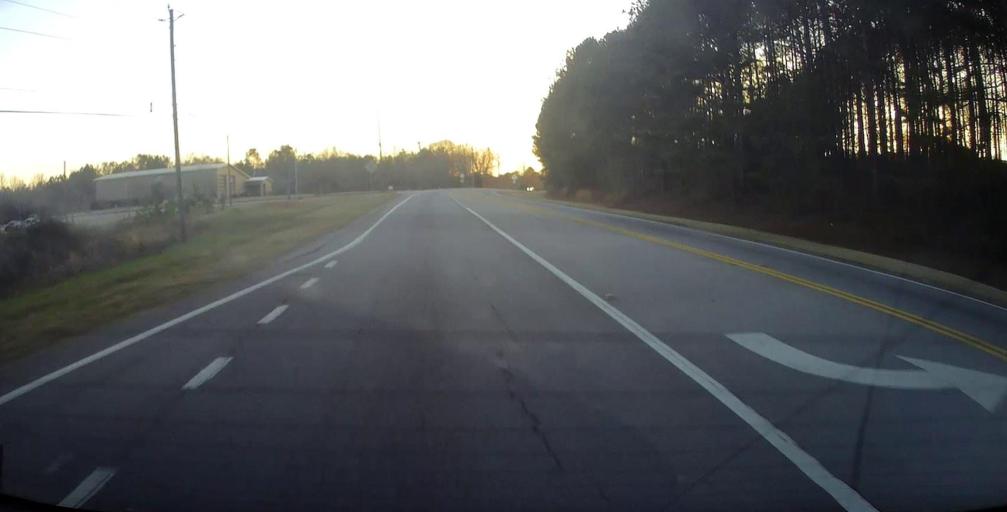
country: US
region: Georgia
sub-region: Troup County
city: La Grange
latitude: 33.0203
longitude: -84.9945
